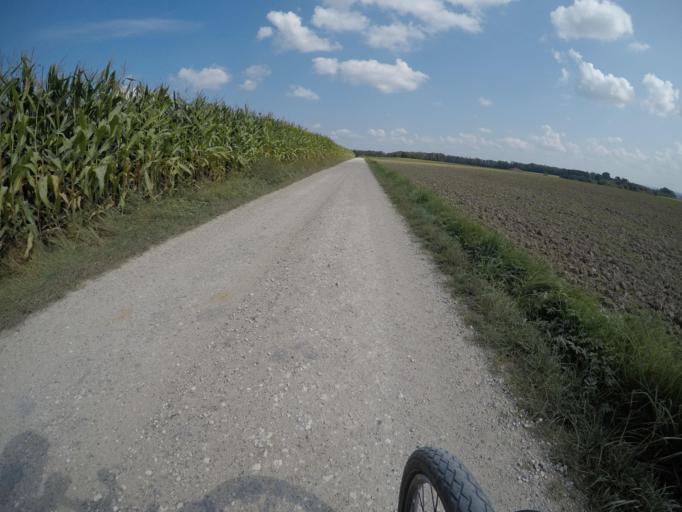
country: DE
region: Bavaria
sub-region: Swabia
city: Biberbach
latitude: 48.5418
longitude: 10.7934
